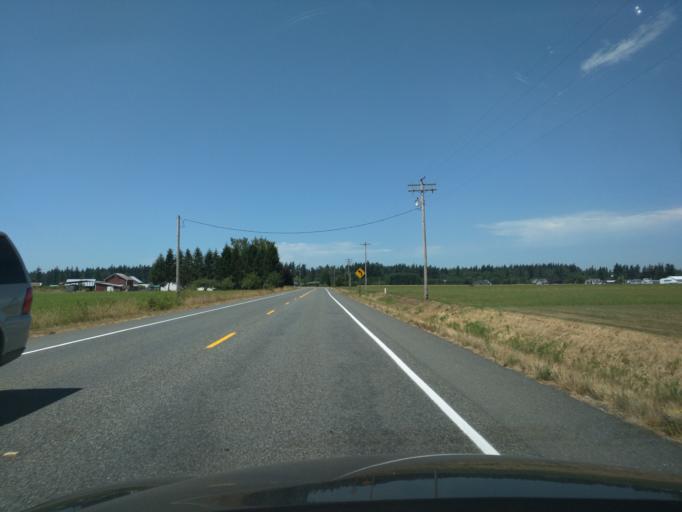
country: US
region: Washington
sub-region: Whatcom County
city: Lynden
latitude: 48.9649
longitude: -122.4922
